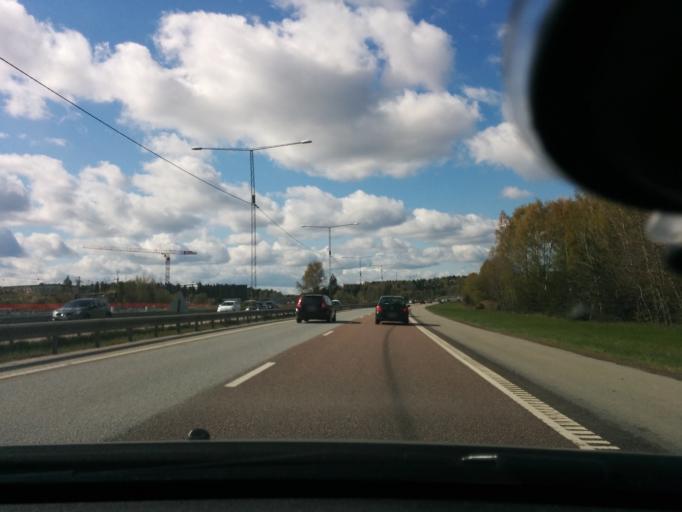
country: SE
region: Stockholm
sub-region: Jarfalla Kommun
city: Jakobsberg
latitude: 59.4061
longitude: 17.8637
